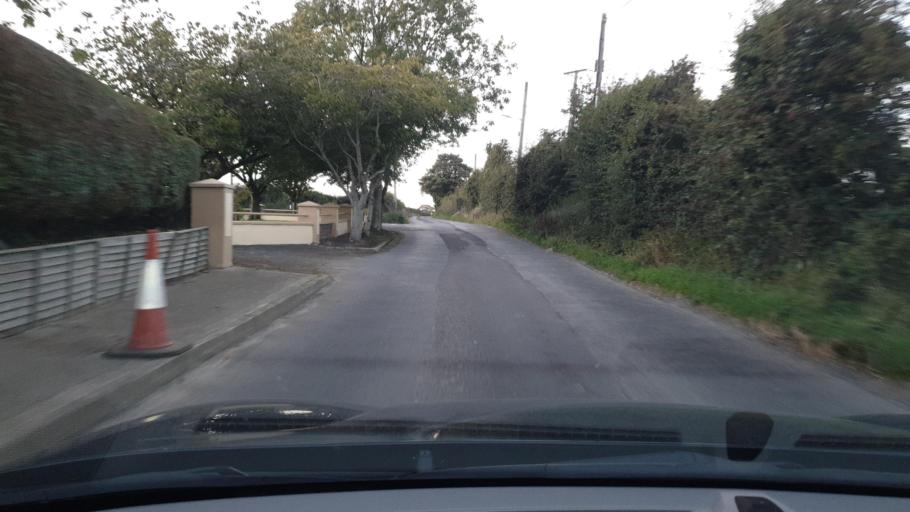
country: IE
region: Leinster
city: Balrothery
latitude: 53.5754
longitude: -6.1659
